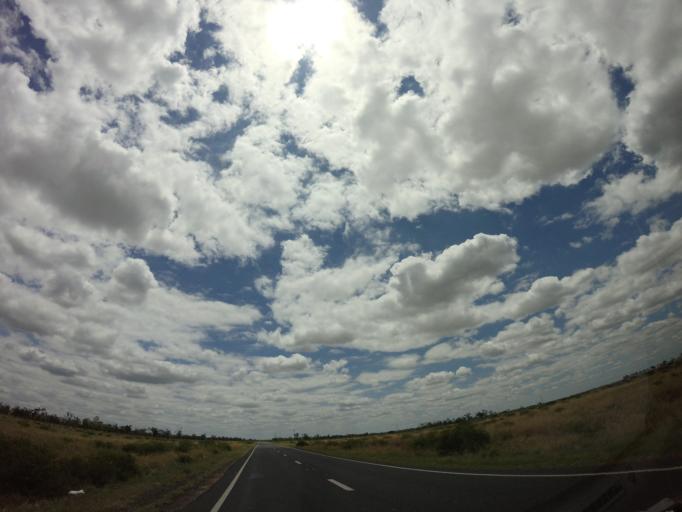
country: AU
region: New South Wales
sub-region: Moree Plains
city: Boggabilla
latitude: -28.6690
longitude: 150.3182
